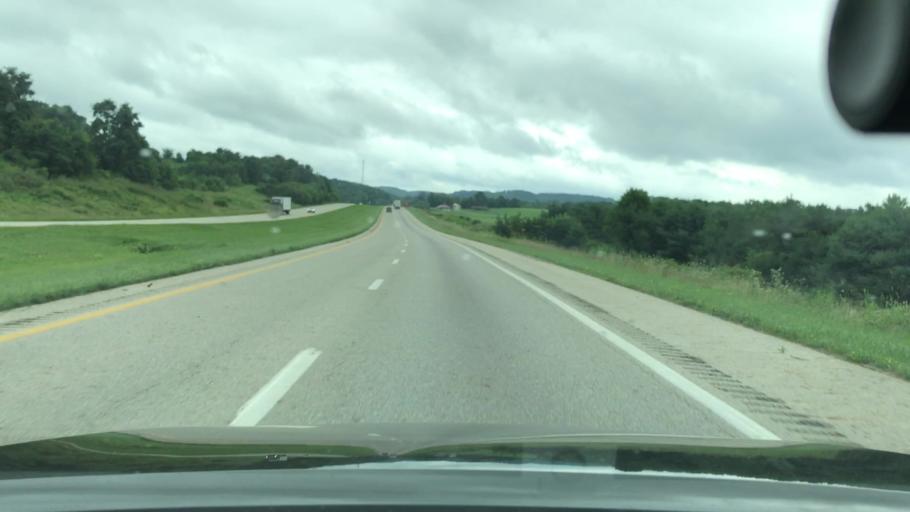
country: US
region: Ohio
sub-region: Ross County
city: Chillicothe
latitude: 39.2631
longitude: -82.8678
